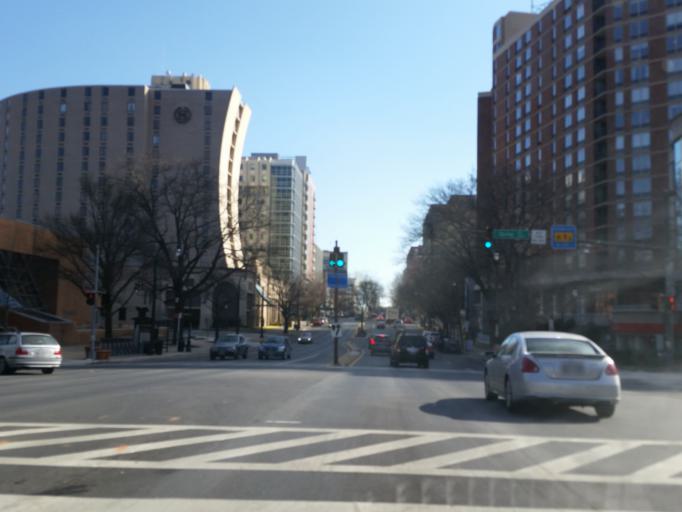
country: US
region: Maryland
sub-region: Montgomery County
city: Silver Spring
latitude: 38.9996
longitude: -77.0321
